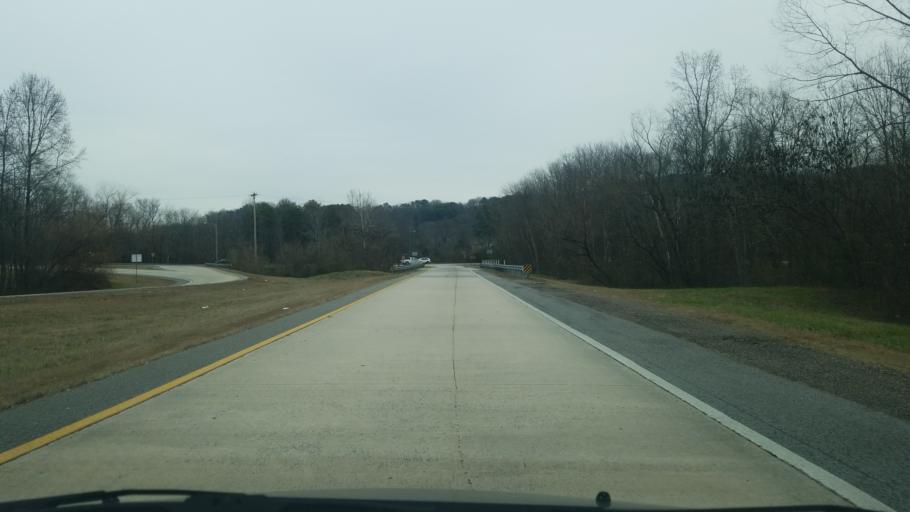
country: US
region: Tennessee
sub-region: Hamilton County
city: Soddy-Daisy
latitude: 35.2324
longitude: -85.1967
